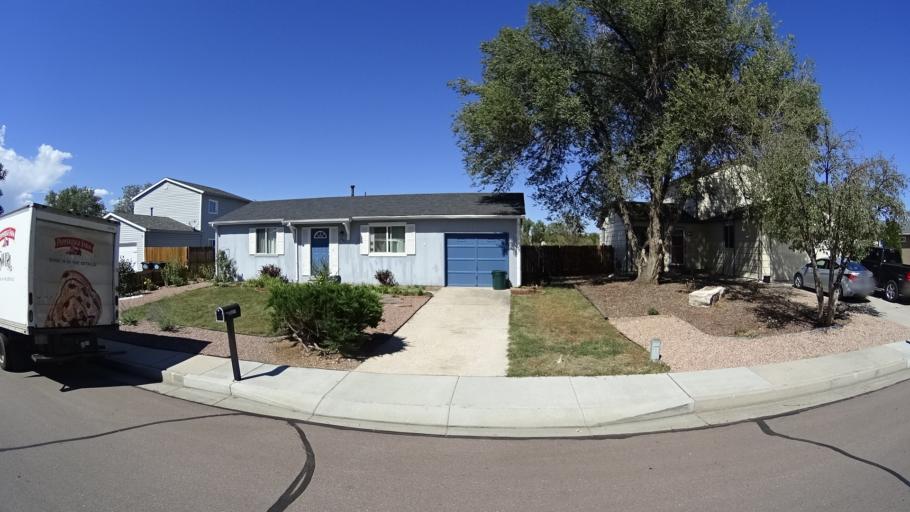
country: US
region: Colorado
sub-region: El Paso County
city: Stratmoor
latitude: 38.7864
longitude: -104.7440
